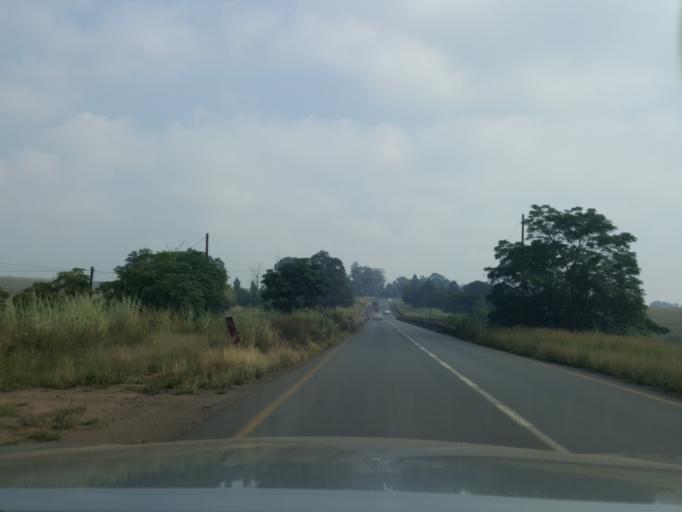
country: ZA
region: Mpumalanga
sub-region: Nkangala District Municipality
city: Witbank
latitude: -26.0022
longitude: 29.2932
